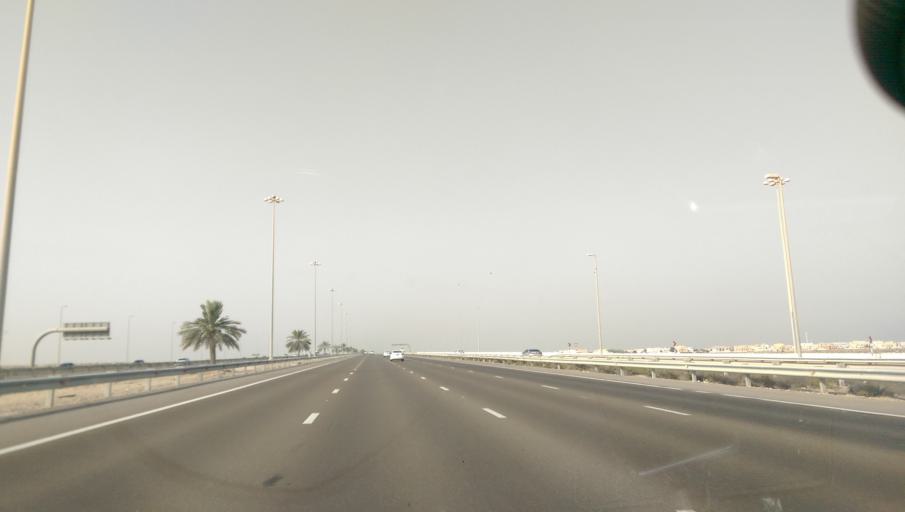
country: AE
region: Abu Dhabi
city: Abu Dhabi
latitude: 24.4041
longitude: 54.6702
